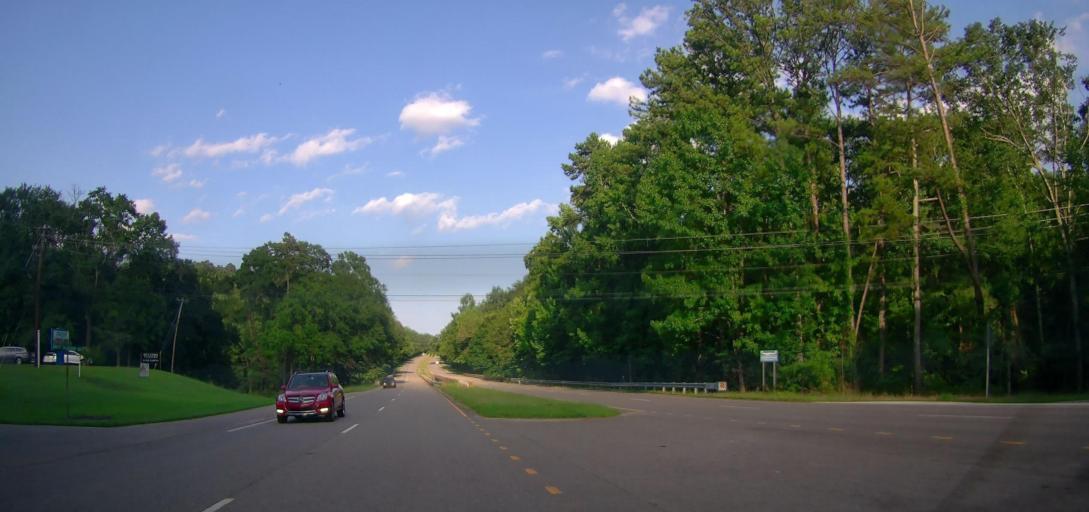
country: US
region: Alabama
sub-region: Jefferson County
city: Leeds
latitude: 33.5460
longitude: -86.6144
